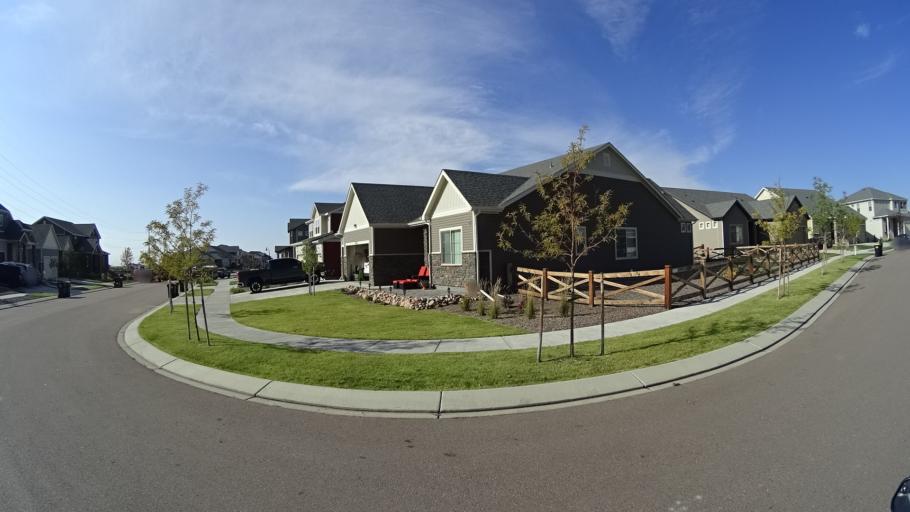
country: US
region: Colorado
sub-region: El Paso County
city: Cimarron Hills
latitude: 38.9296
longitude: -104.6643
